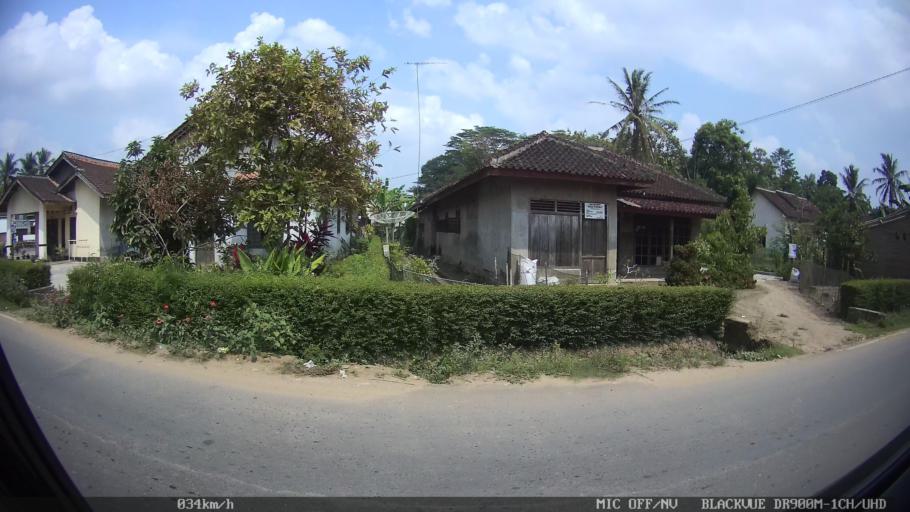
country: ID
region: Lampung
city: Pringsewu
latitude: -5.3870
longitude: 104.9693
